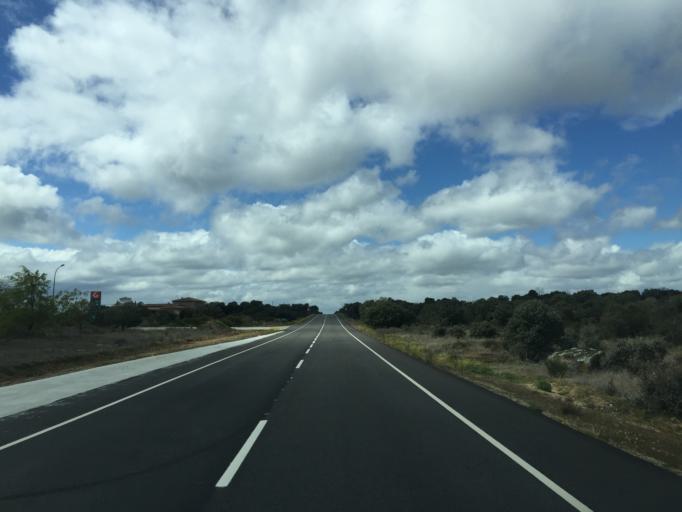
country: ES
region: Castille and Leon
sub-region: Provincia de Zamora
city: Torregamones
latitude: 41.4793
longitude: -6.1790
